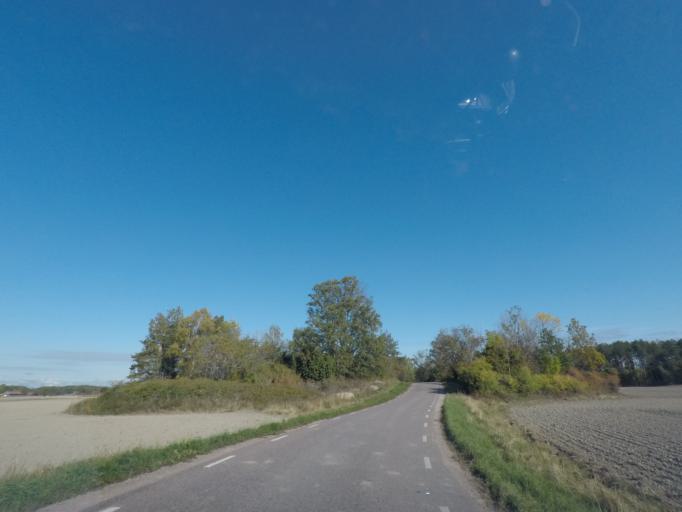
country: SE
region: Vaestmanland
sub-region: Vasteras
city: Vasteras
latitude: 59.5700
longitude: 16.4538
